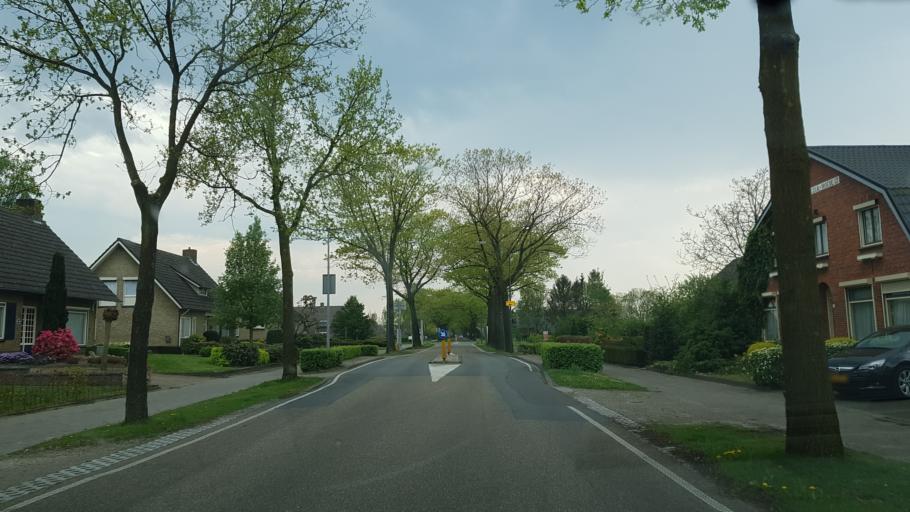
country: NL
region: North Brabant
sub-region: Gemeente Someren
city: Someren
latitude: 51.3471
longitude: 5.6955
